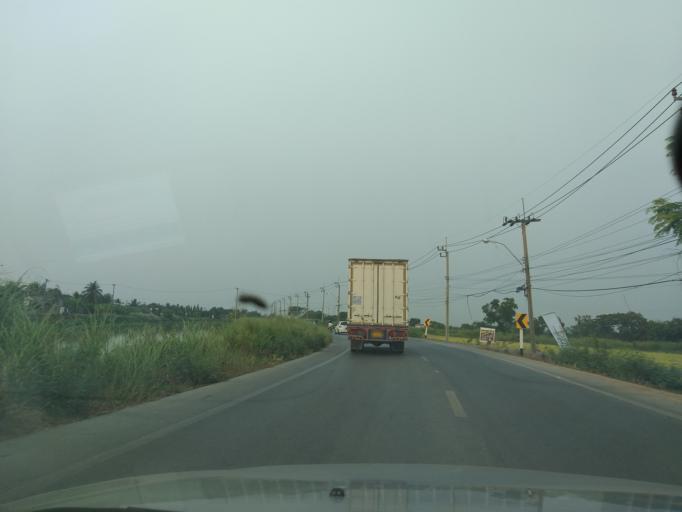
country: TH
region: Bangkok
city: Nong Chok
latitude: 13.8644
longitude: 100.8743
